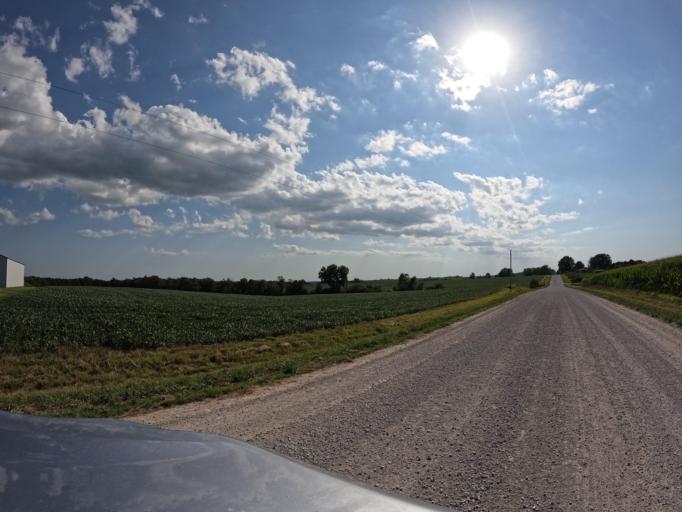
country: US
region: Iowa
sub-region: Appanoose County
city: Centerville
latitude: 40.7179
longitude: -93.0138
